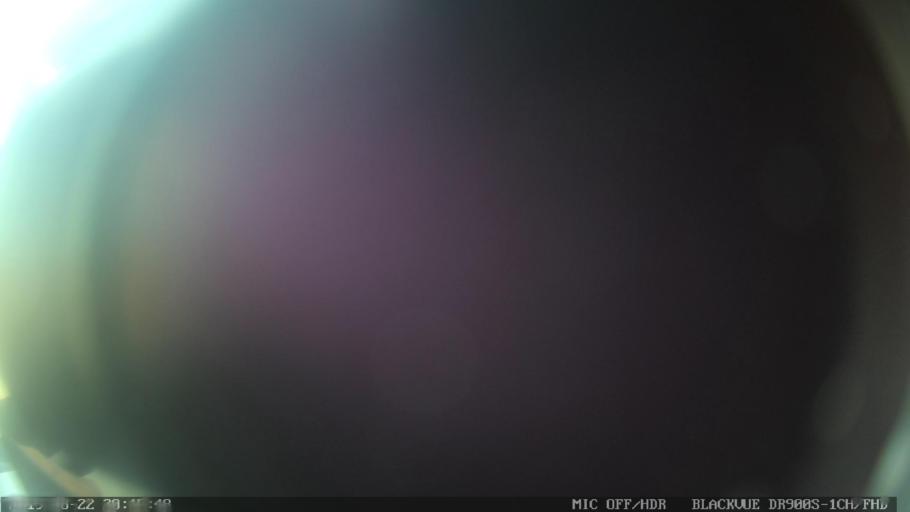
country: PT
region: Guarda
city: Alcains
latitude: 39.9232
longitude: -7.4452
